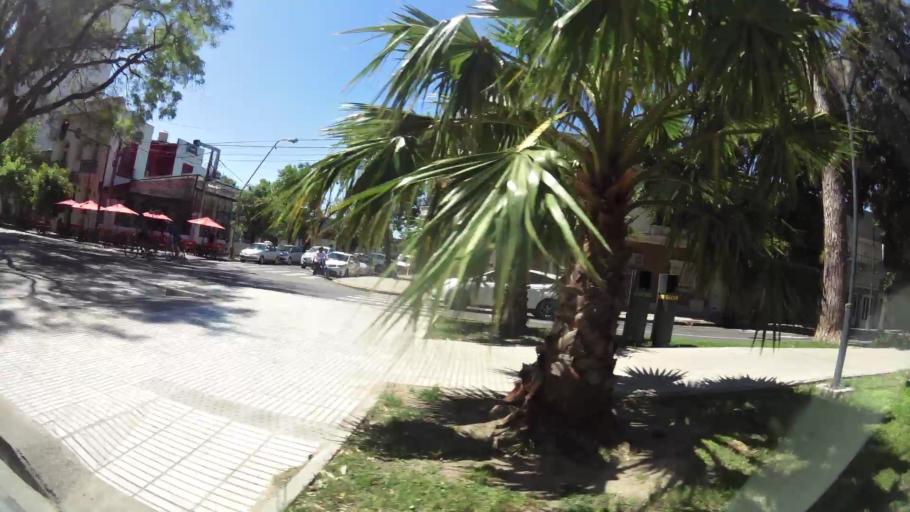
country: AR
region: Santa Fe
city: Santa Fe de la Vera Cruz
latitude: -31.6378
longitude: -60.6932
